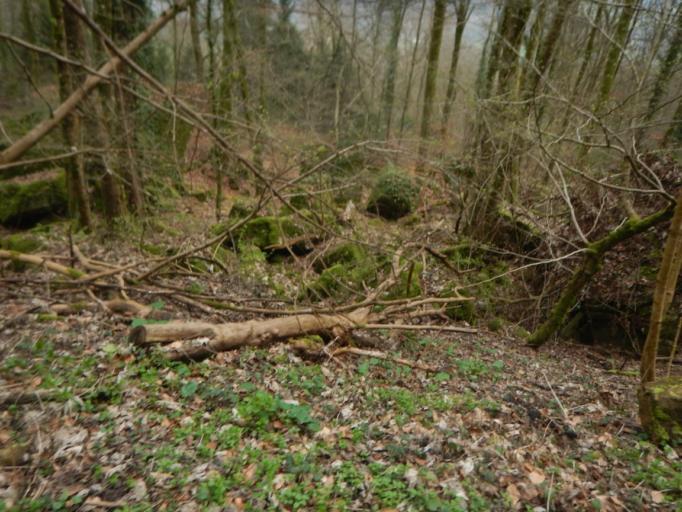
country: LU
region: Grevenmacher
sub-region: Canton d'Echternach
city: Beaufort
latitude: 49.8431
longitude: 6.3143
